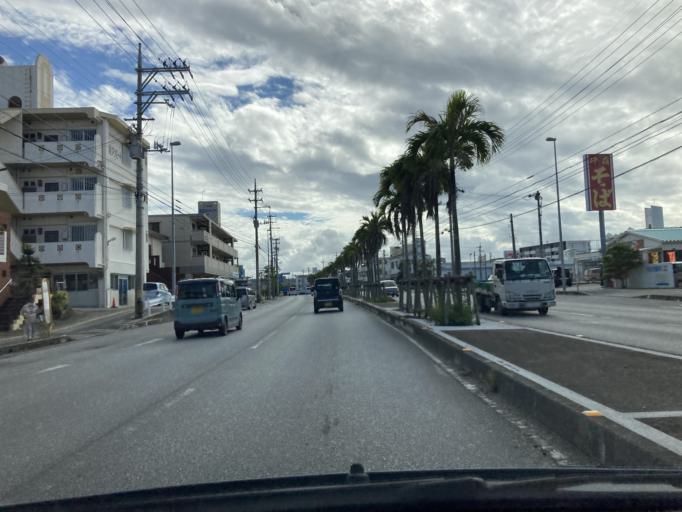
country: JP
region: Okinawa
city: Tomigusuku
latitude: 26.1596
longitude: 127.7222
